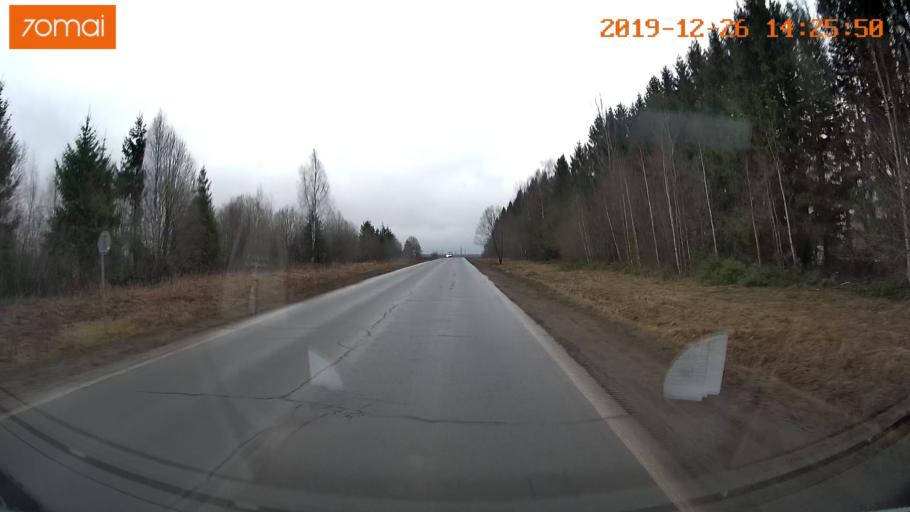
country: RU
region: Jaroslavl
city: Poshekhon'ye
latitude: 58.4913
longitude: 39.0907
